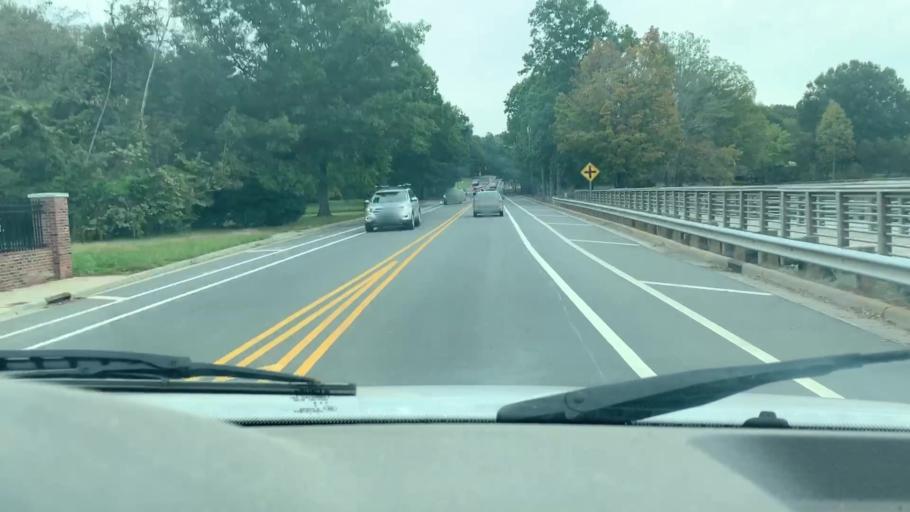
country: US
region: North Carolina
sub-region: Gaston County
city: Davidson
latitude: 35.5029
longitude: -80.8552
